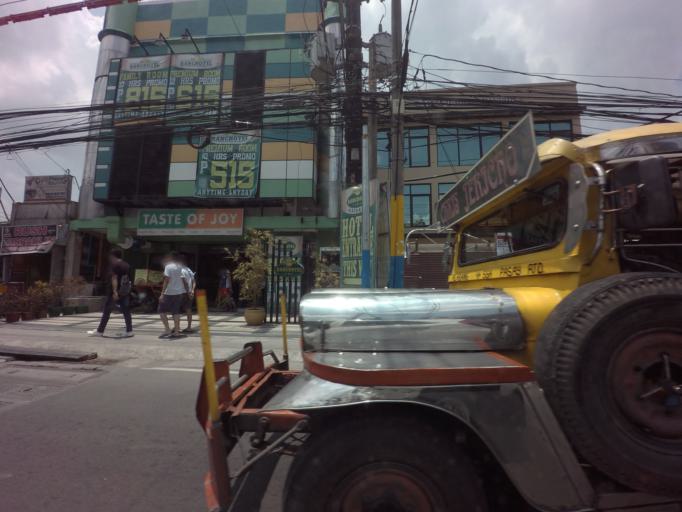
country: PH
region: Calabarzon
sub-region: Province of Laguna
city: San Pedro
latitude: 14.4091
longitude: 121.0465
